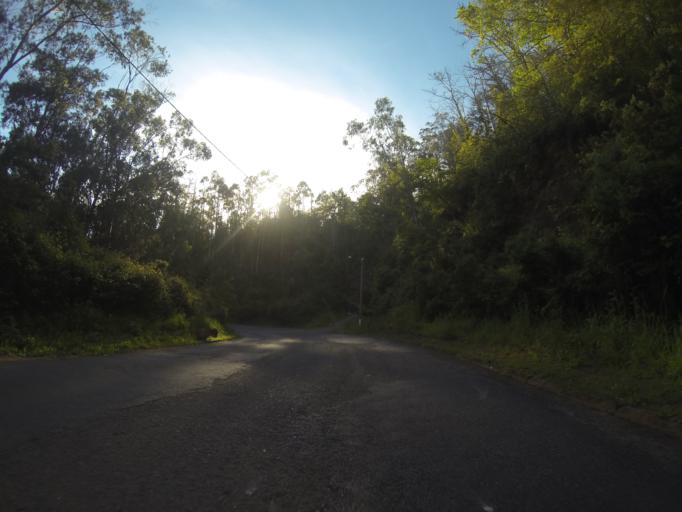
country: PT
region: Madeira
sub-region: Santa Cruz
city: Camacha
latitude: 32.6718
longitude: -16.8676
